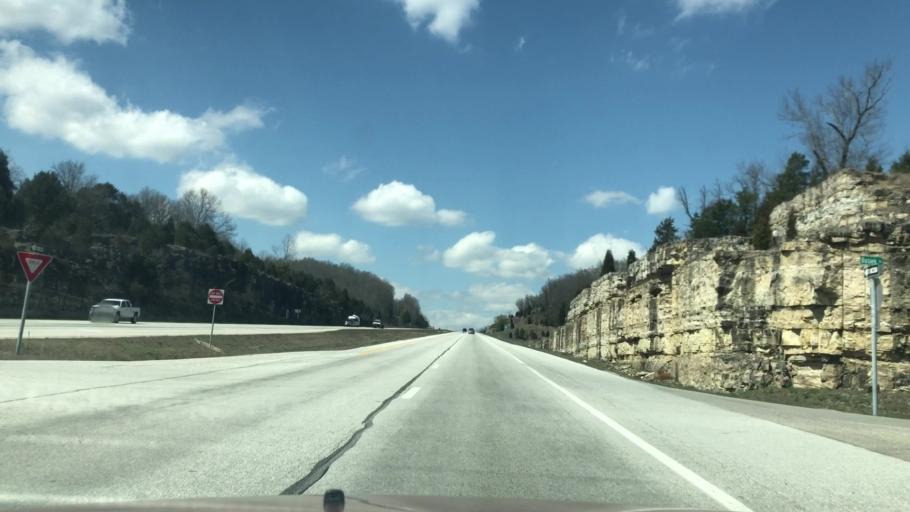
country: US
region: Missouri
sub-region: Christian County
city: Ozark
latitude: 36.8668
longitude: -93.2288
